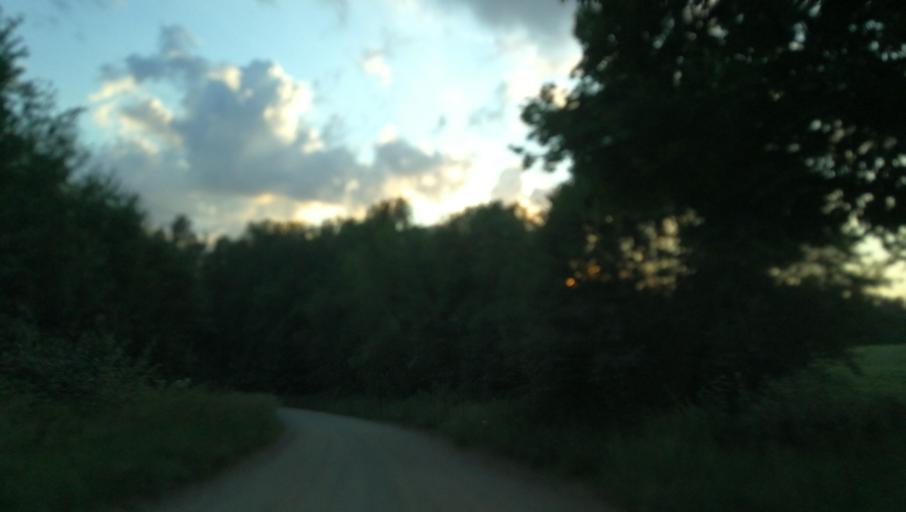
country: LV
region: Ligatne
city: Ligatne
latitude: 57.2602
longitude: 25.1552
